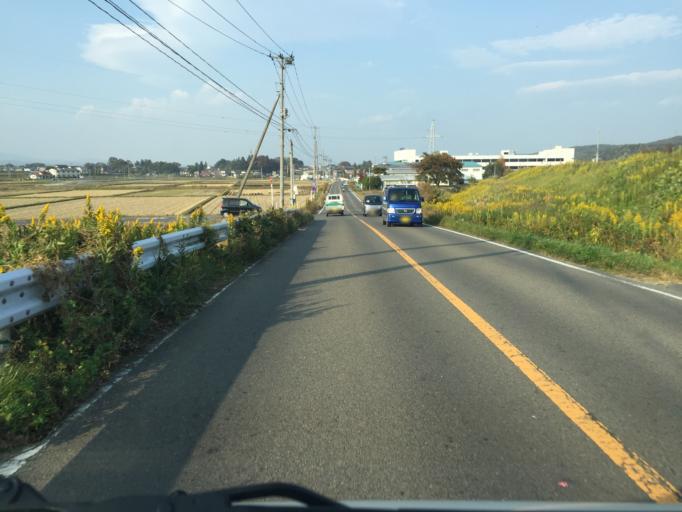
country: JP
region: Fukushima
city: Motomiya
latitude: 37.4835
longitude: 140.3994
